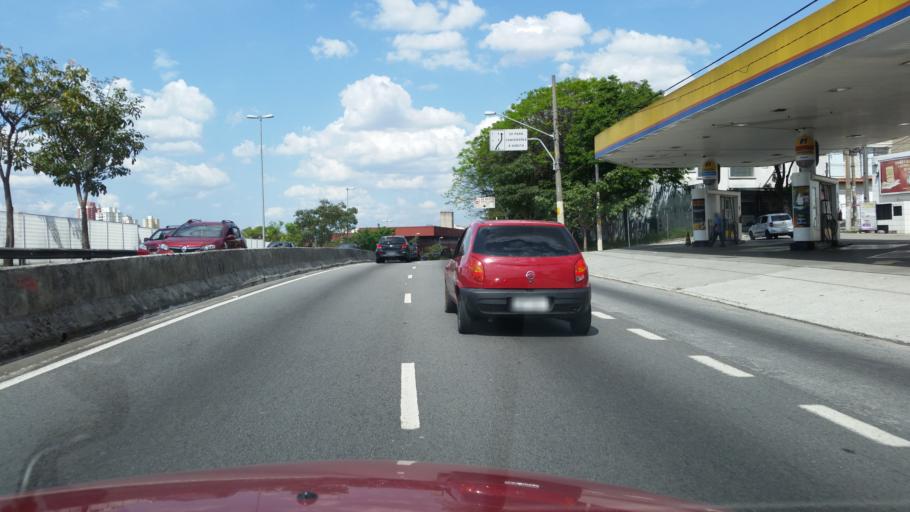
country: BR
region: Sao Paulo
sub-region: Guarulhos
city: Guarulhos
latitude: -23.5320
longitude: -46.5334
